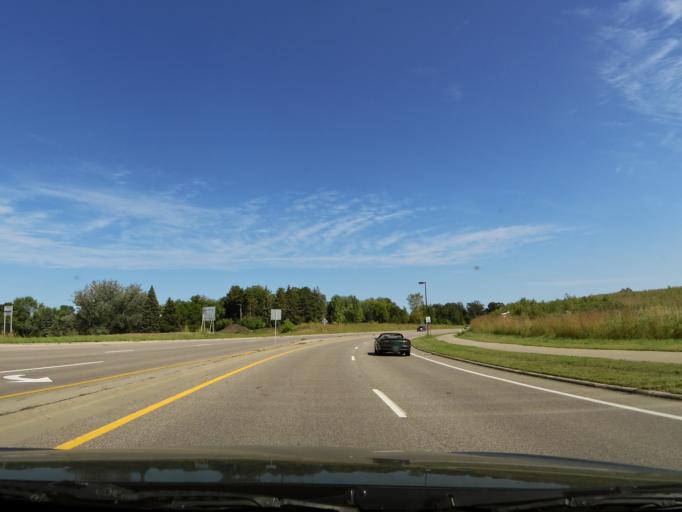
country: US
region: Minnesota
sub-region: Carver County
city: Chanhassen
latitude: 44.8466
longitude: -93.5388
